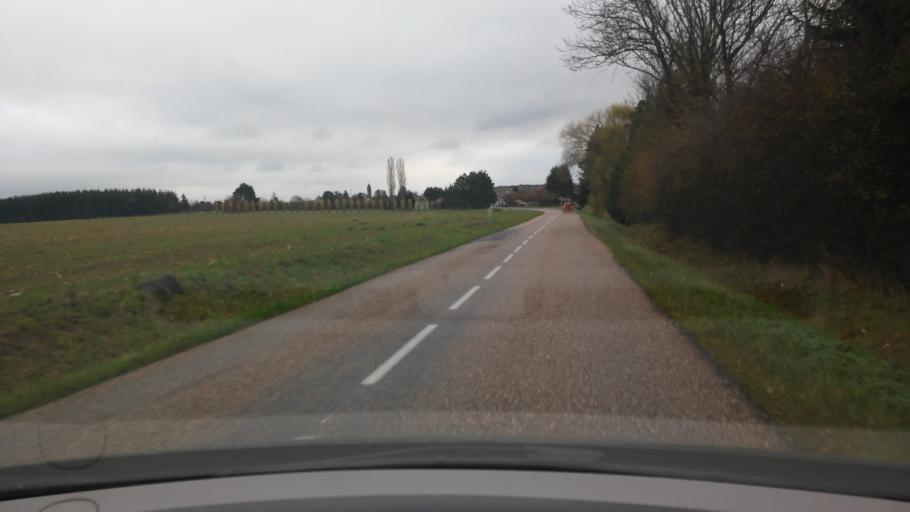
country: FR
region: Lorraine
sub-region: Departement de la Moselle
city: Metzervisse
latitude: 49.2941
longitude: 6.2947
